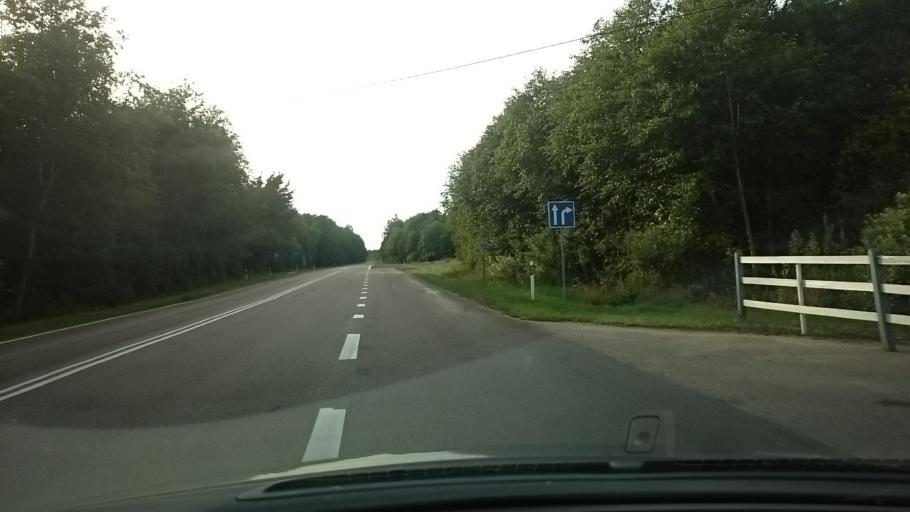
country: EE
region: Saare
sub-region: Kuressaare linn
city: Kuressaare
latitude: 58.2916
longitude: 22.3815
